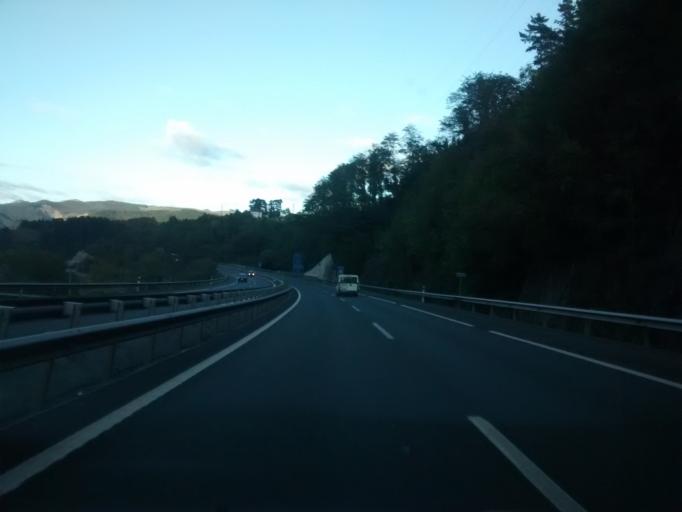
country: ES
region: Basque Country
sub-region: Provincia de Guipuzcoa
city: Elgoibar
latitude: 43.2036
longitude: -2.4251
